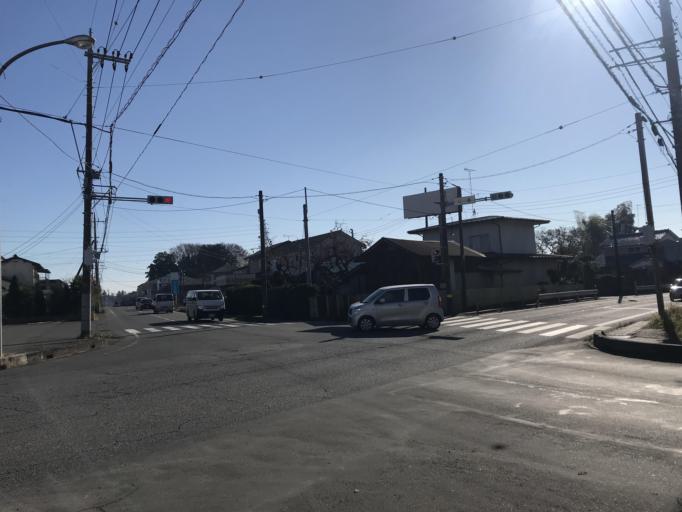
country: JP
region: Ibaraki
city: Sakai
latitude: 36.1836
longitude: 139.8108
